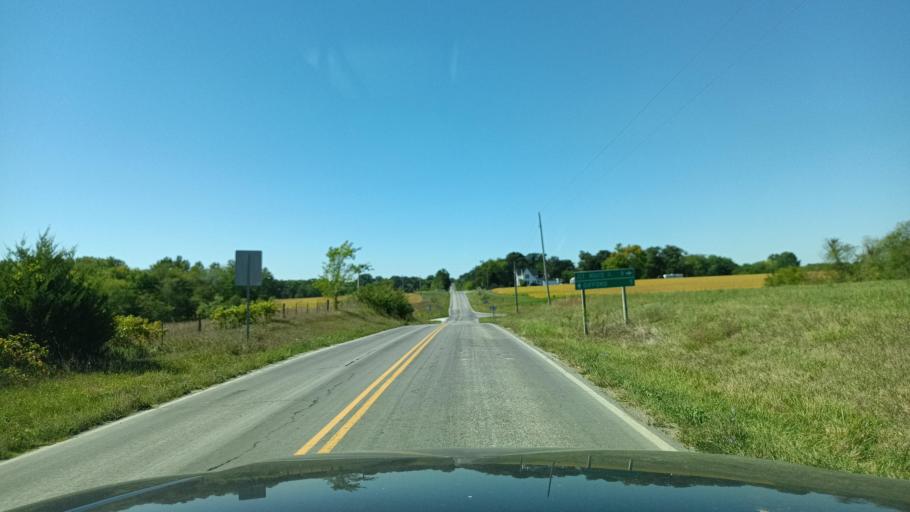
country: US
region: Missouri
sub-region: Macon County
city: La Plata
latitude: 40.0232
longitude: -92.5838
